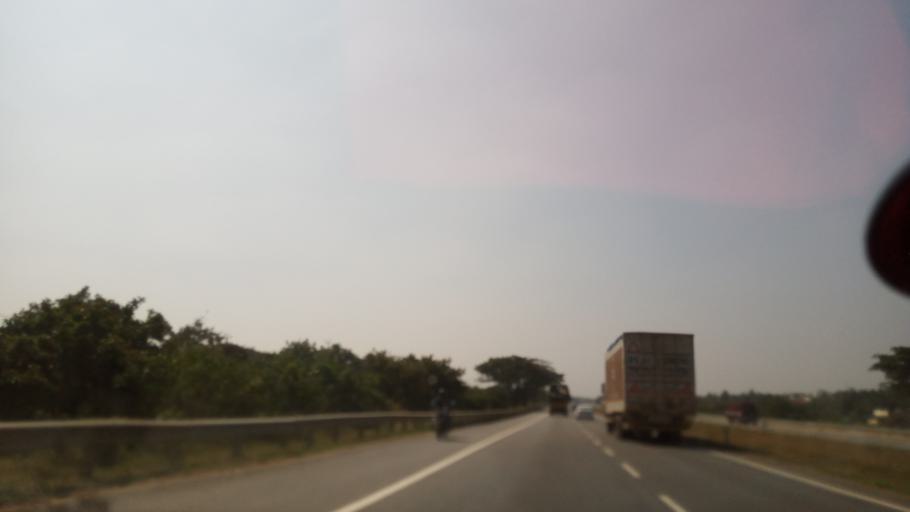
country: IN
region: Karnataka
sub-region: Bangalore Urban
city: Bangalore
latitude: 12.9555
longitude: 77.4714
